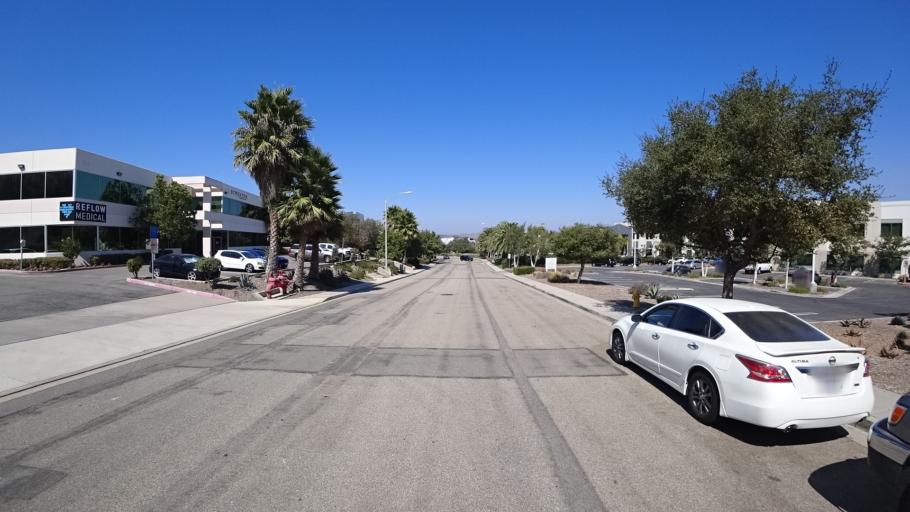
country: US
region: California
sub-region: Orange County
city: San Clemente
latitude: 33.4460
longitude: -117.5875
